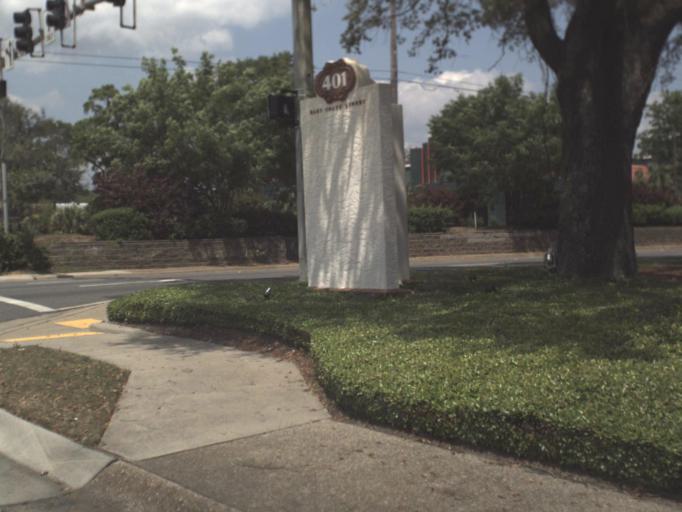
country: US
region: Florida
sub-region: Escambia County
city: Pensacola
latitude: 30.4158
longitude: -87.2054
